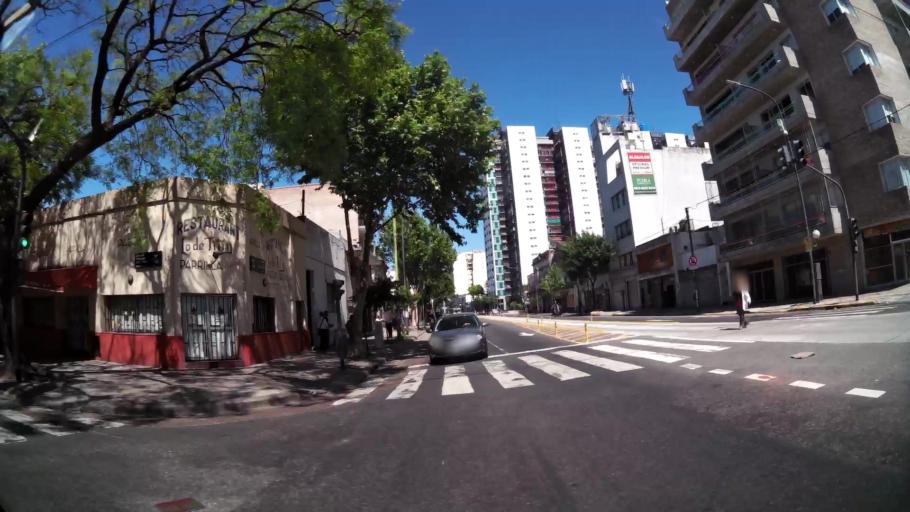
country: AR
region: Buenos Aires F.D.
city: Buenos Aires
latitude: -34.6304
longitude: -58.3963
